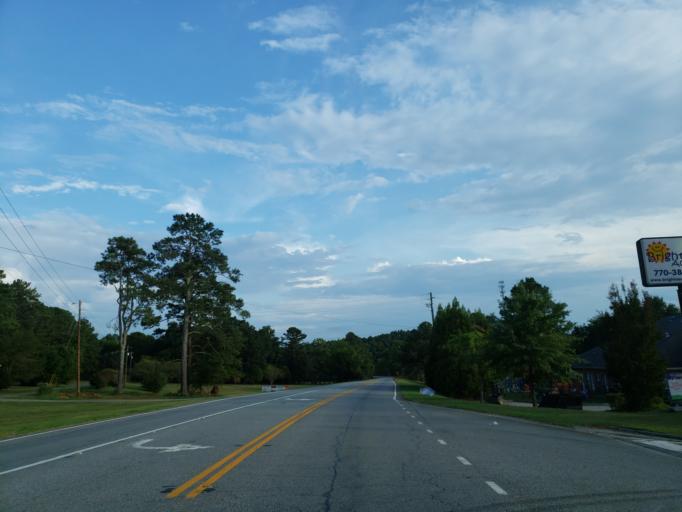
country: US
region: Georgia
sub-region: Bartow County
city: Cartersville
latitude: 34.2244
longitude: -84.8560
